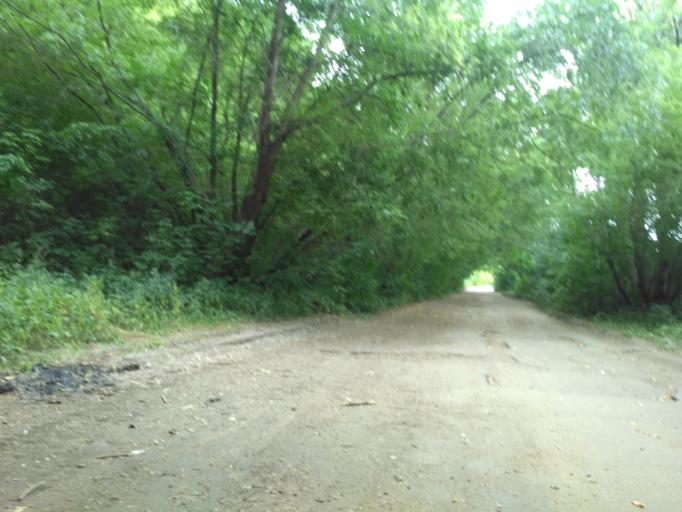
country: RU
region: Nizjnij Novgorod
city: Nizhniy Novgorod
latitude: 56.2898
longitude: 43.9687
